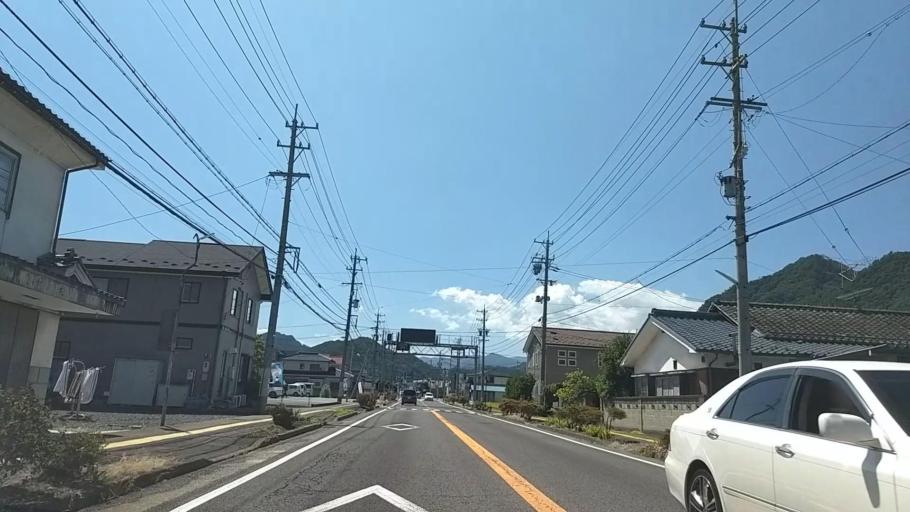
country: JP
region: Nagano
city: Kamimaruko
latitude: 36.3348
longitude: 138.2720
